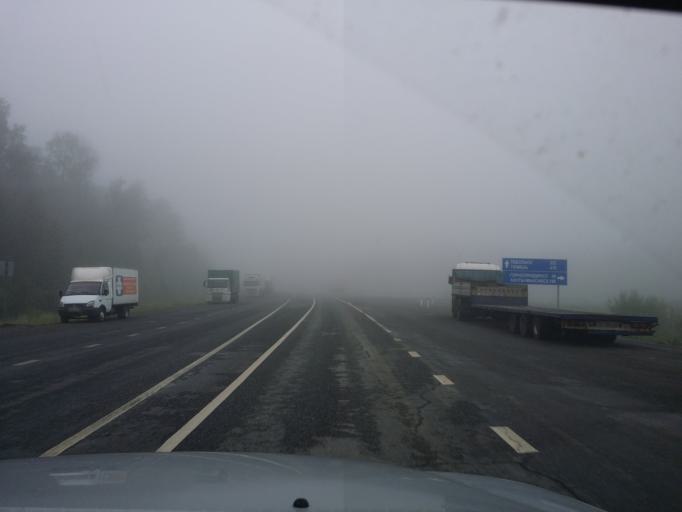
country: RU
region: Khanty-Mansiyskiy Avtonomnyy Okrug
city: Gornopravdinsk
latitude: 59.6927
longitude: 70.0925
